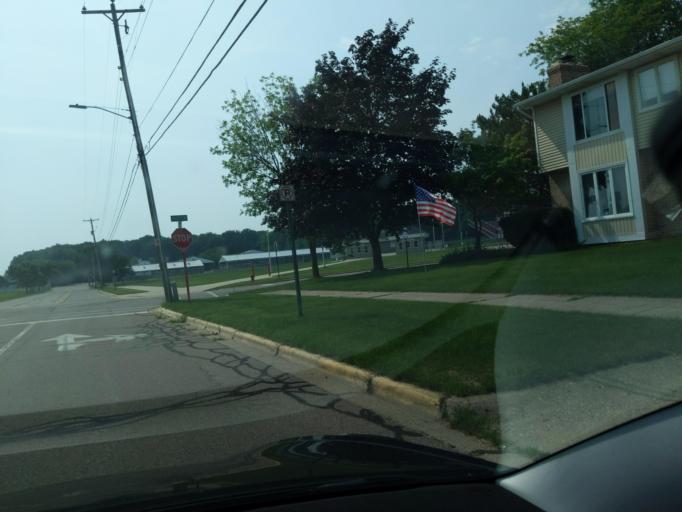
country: US
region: Michigan
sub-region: Clinton County
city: Saint Johns
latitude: 42.9931
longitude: -84.5659
